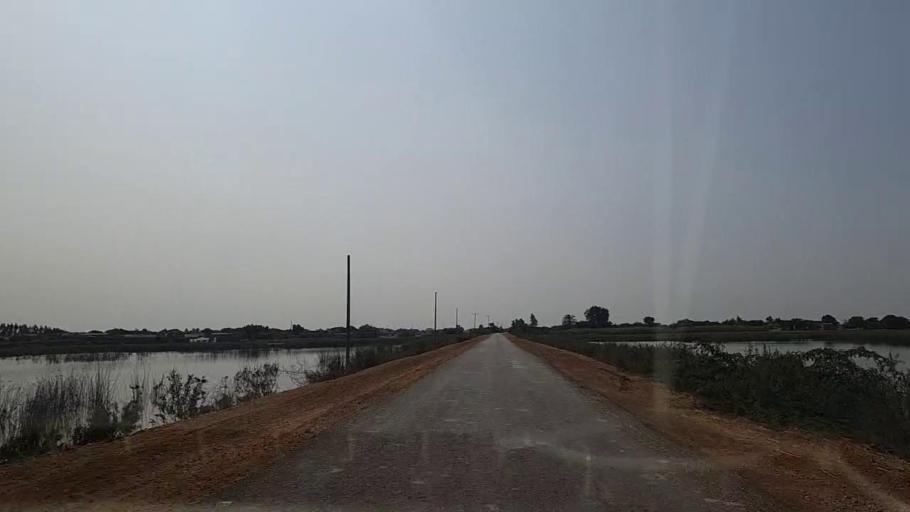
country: PK
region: Sindh
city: Chuhar Jamali
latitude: 24.3079
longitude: 67.9376
